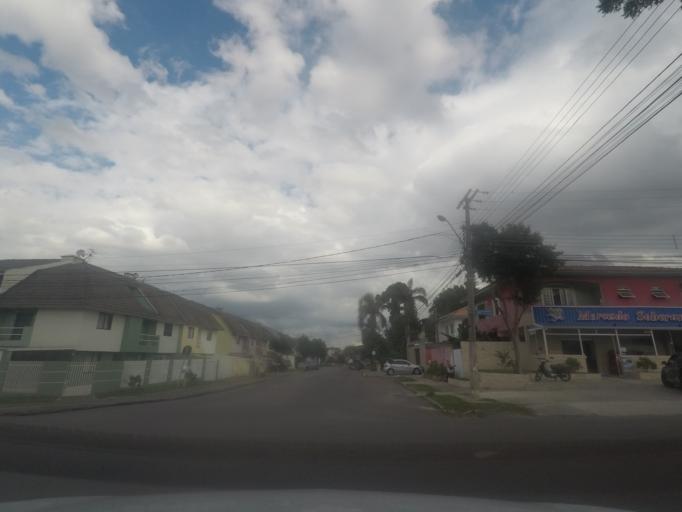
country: BR
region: Parana
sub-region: Pinhais
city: Pinhais
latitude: -25.4644
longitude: -49.2192
